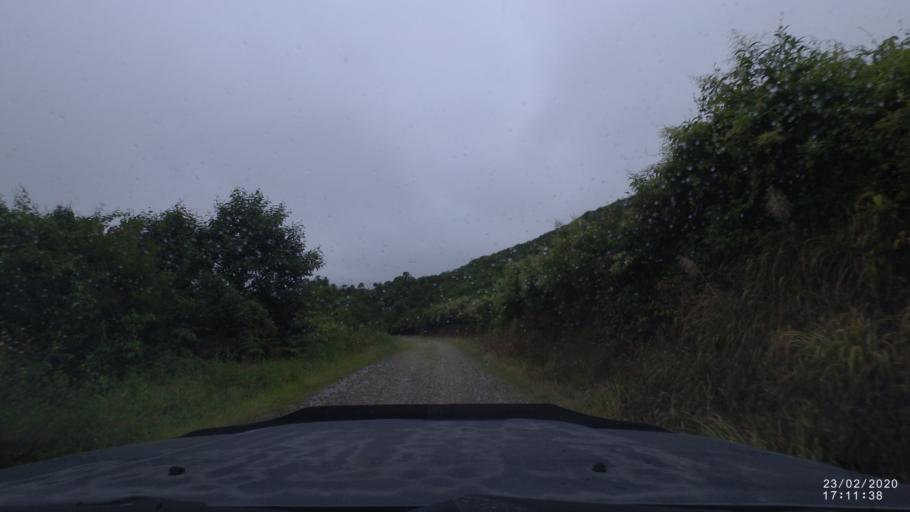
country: BO
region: Cochabamba
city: Colomi
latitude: -17.1332
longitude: -65.9449
